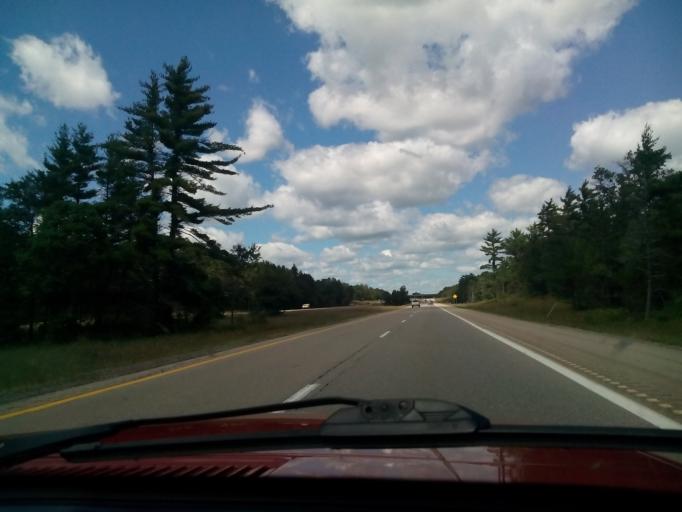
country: US
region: Michigan
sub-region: Crawford County
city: Grayling
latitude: 44.6621
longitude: -84.6971
